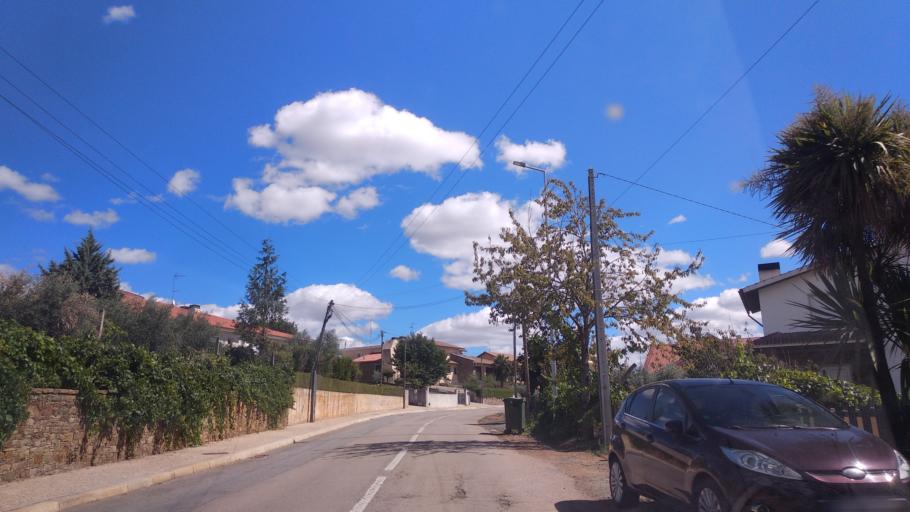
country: PT
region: Braganca
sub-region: Braganca Municipality
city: Braganca
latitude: 41.7859
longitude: -6.7674
